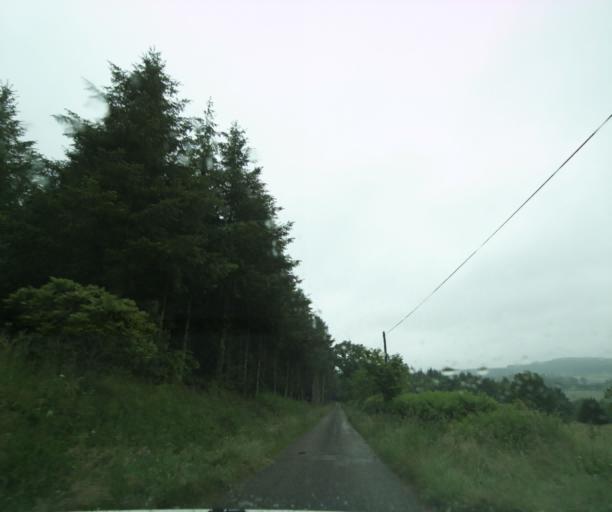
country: FR
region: Bourgogne
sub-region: Departement de Saone-et-Loire
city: La Clayette
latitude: 46.3682
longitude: 4.3670
